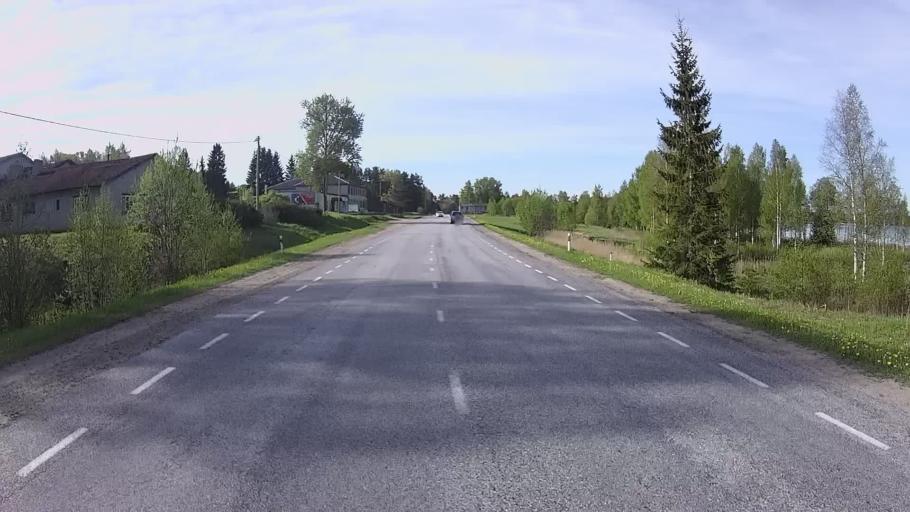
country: EE
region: Tartu
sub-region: Elva linn
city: Elva
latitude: 58.1310
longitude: 26.5227
